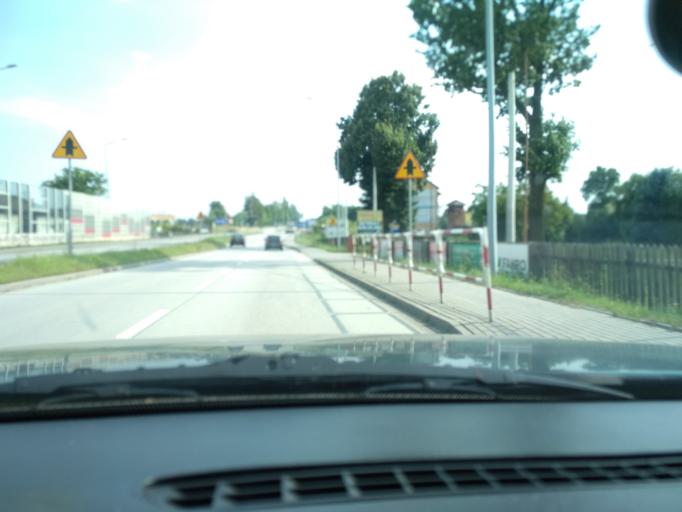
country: PL
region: Silesian Voivodeship
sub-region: Zory
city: Zory
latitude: 50.0242
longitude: 18.7074
